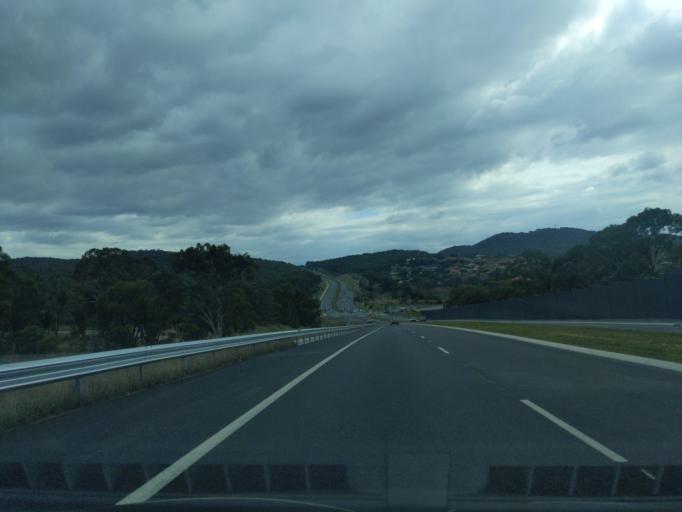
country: AU
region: New South Wales
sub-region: Queanbeyan
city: Queanbeyan
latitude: -35.3785
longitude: 149.2401
